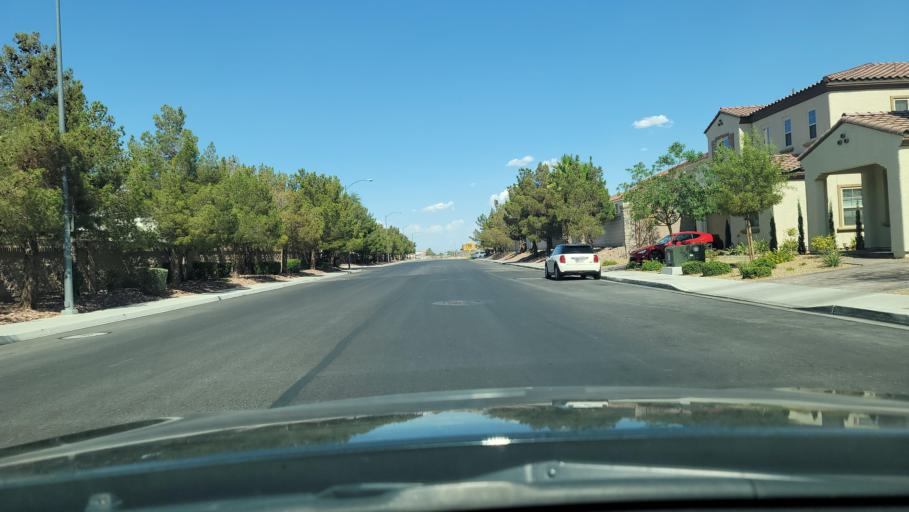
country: US
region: Nevada
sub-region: Clark County
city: Spring Valley
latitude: 36.0814
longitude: -115.2741
